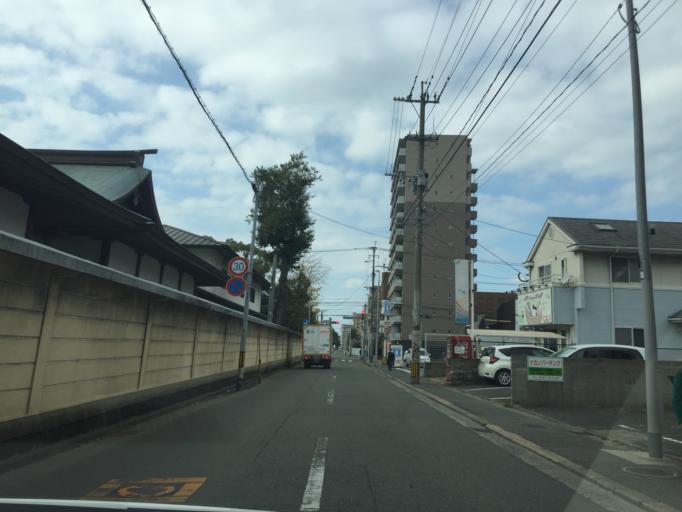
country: JP
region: Fukuoka
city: Fukuoka-shi
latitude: 33.6152
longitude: 130.4233
